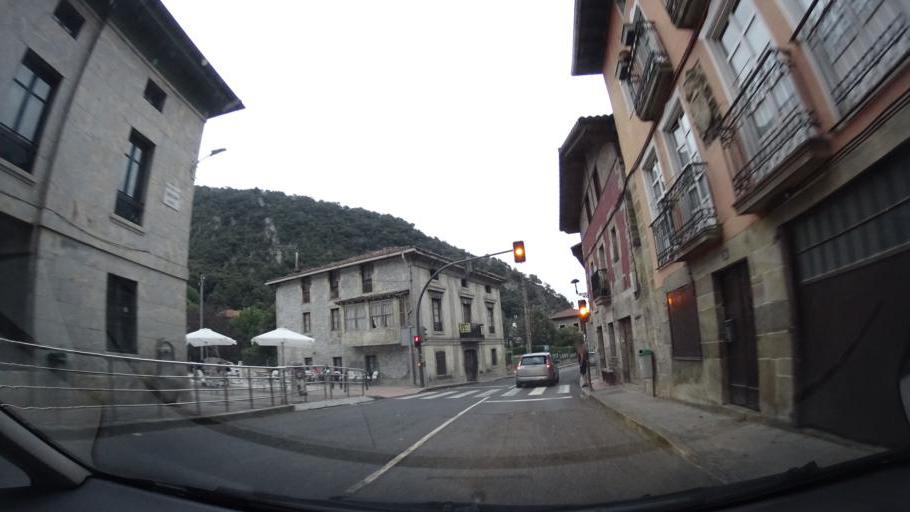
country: ES
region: Basque Country
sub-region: Bizkaia
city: Manaria
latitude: 43.1379
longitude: -2.6606
